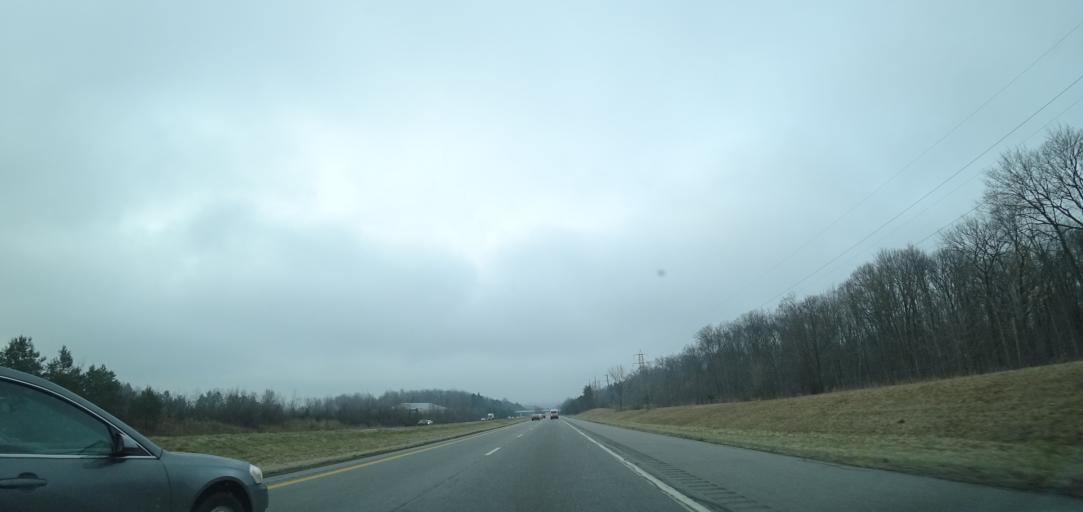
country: US
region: Ohio
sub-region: Summit County
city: Montrose-Ghent
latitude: 41.1811
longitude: -81.6260
